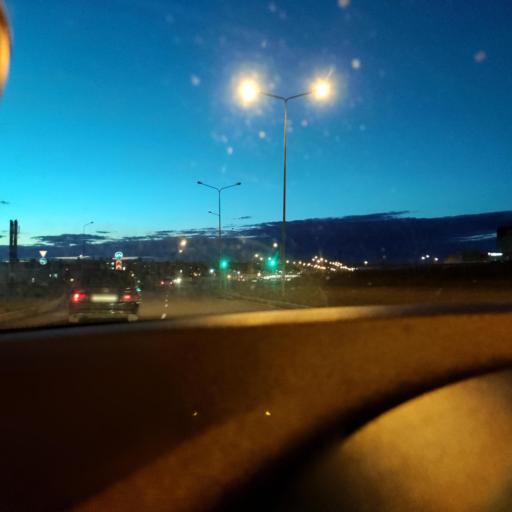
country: RU
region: Samara
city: Petra-Dubrava
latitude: 53.2947
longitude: 50.3284
